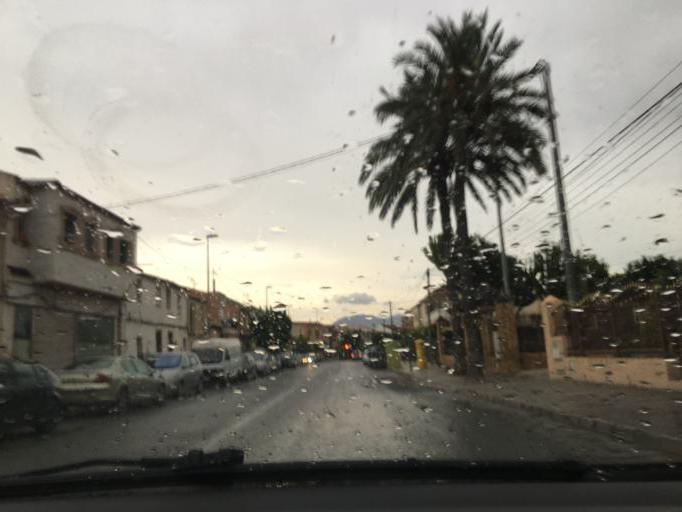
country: ES
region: Murcia
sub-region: Murcia
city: Santomera
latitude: 38.0300
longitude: -1.0449
